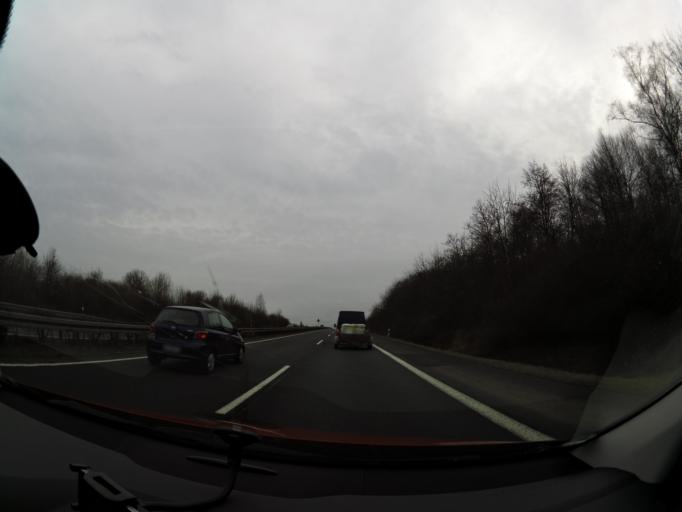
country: DE
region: Lower Saxony
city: Gielde
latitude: 52.0387
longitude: 10.5139
